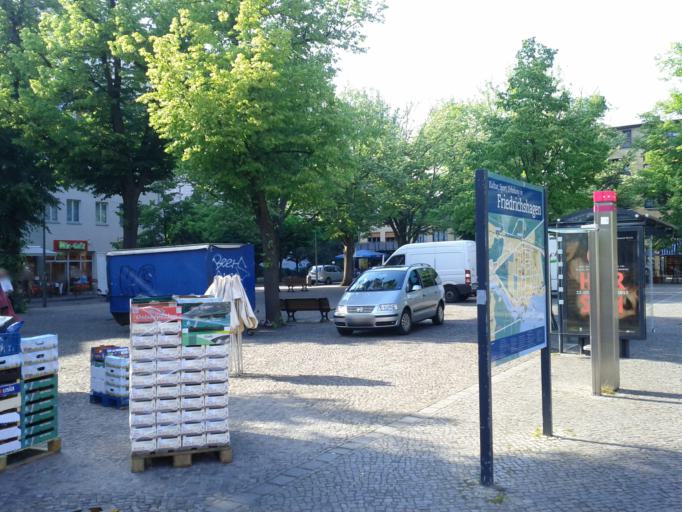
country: DE
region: Berlin
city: Friedrichshagen
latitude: 52.4506
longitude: 13.6245
